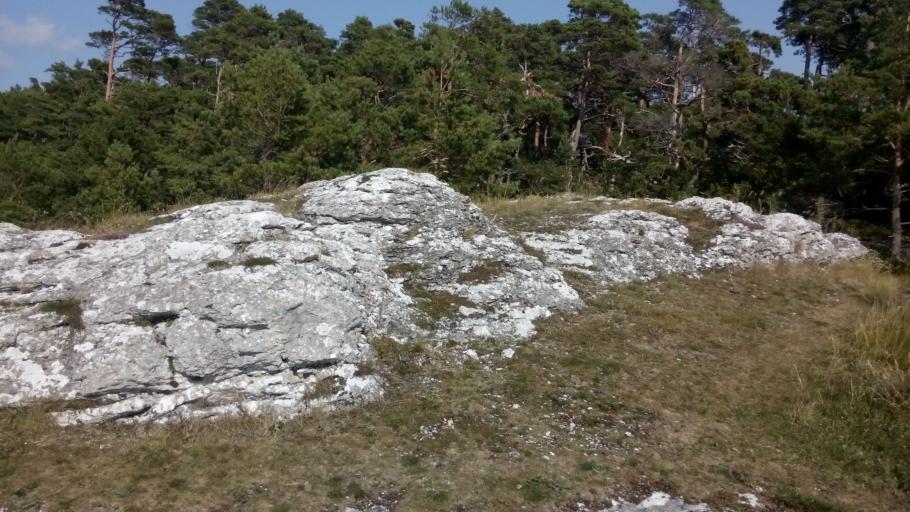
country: SE
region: Gotland
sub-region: Gotland
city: Visby
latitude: 57.7812
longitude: 18.4264
